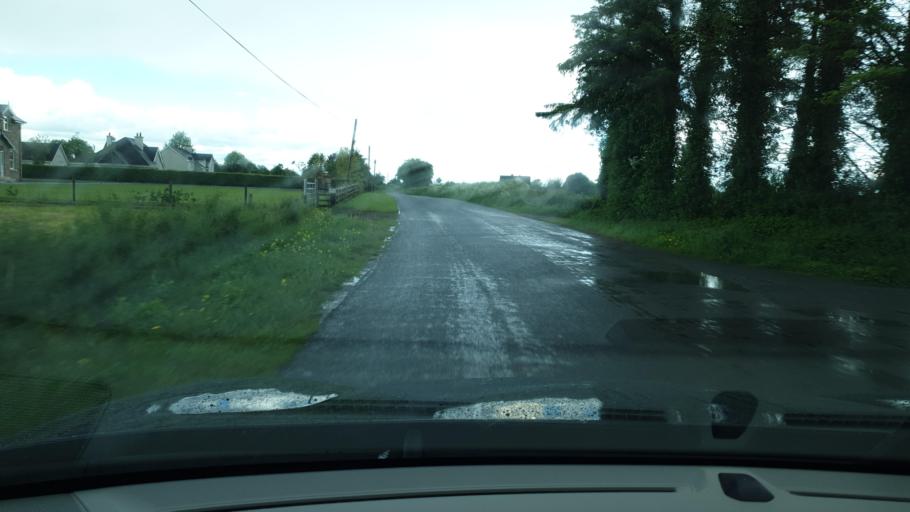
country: IE
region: Leinster
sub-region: Laois
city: Mountmellick
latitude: 53.1208
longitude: -7.3784
